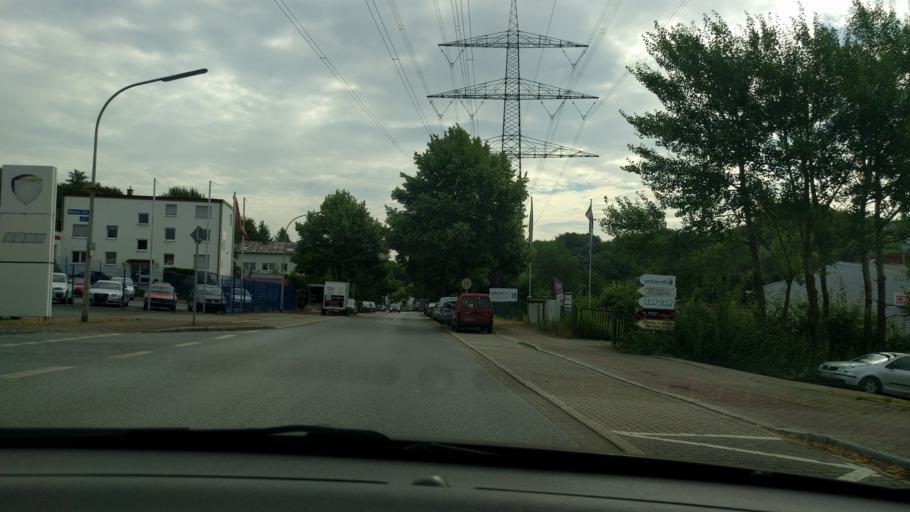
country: DE
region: North Rhine-Westphalia
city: Witten
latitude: 51.4573
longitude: 7.3620
